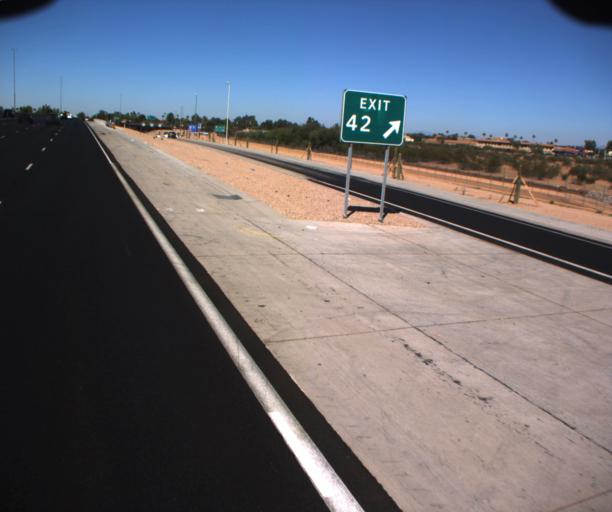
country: US
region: Arizona
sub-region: Maricopa County
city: Scottsdale
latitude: 33.5628
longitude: -111.8853
